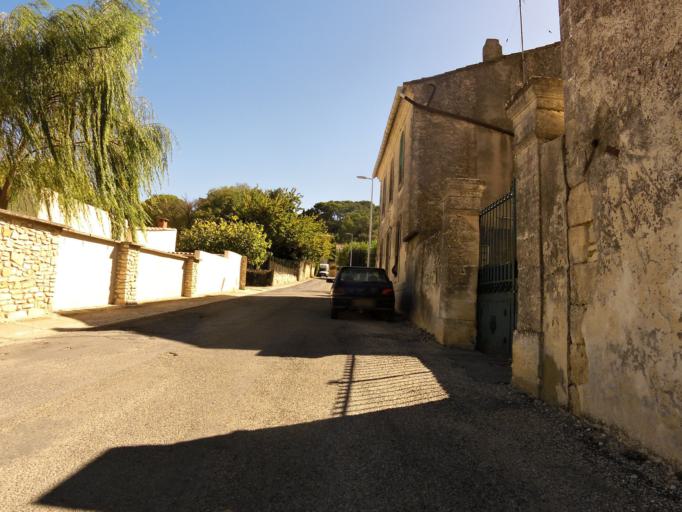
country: FR
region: Languedoc-Roussillon
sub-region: Departement du Gard
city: Nages-et-Solorgues
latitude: 43.7750
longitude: 4.2309
